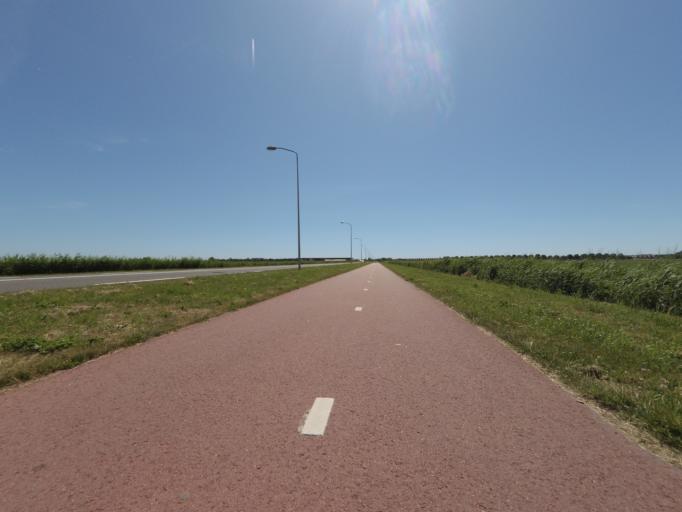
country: NL
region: Flevoland
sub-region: Gemeente Zeewolde
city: Zeewolde
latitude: 52.3503
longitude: 5.5086
